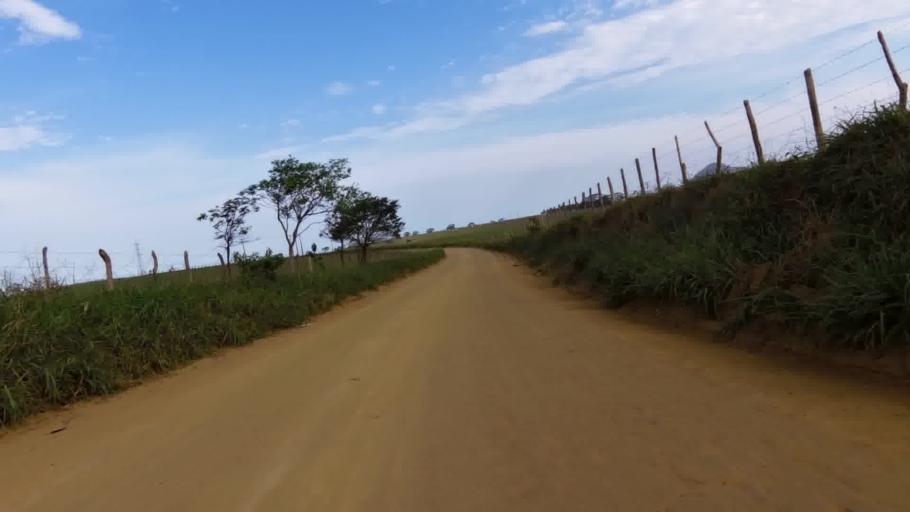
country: BR
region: Espirito Santo
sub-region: Piuma
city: Piuma
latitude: -20.8249
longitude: -40.7465
